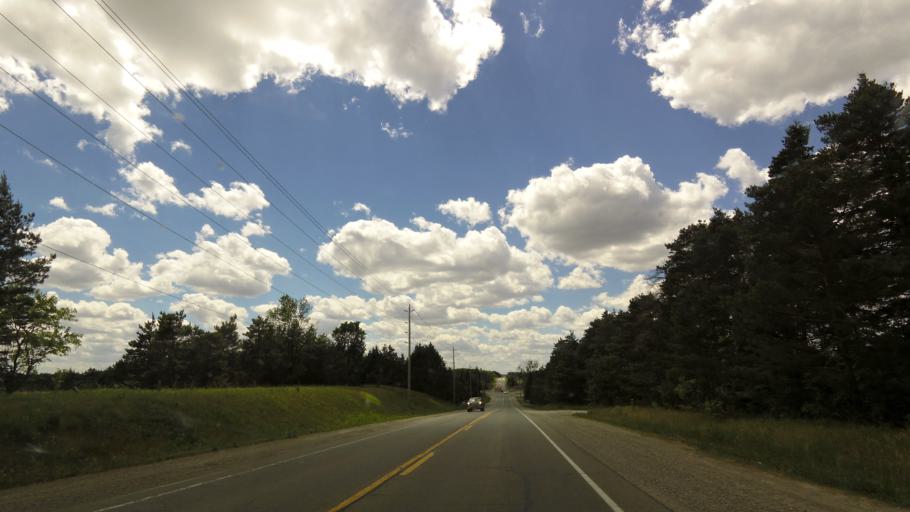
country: CA
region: Ontario
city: Uxbridge
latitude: 44.0467
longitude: -79.1425
